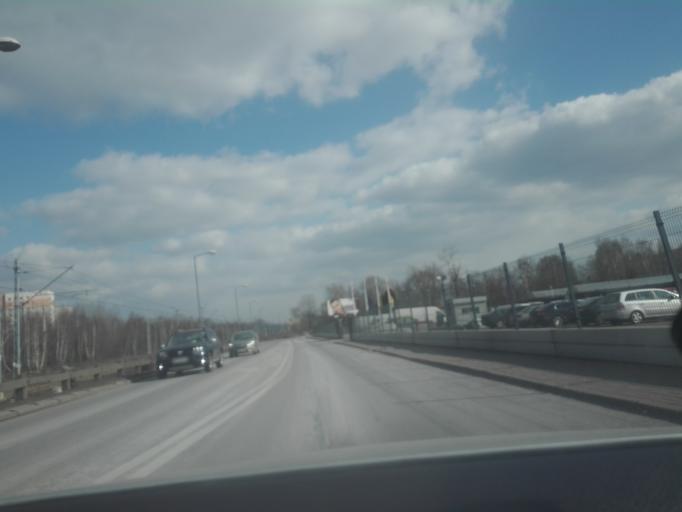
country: PL
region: Silesian Voivodeship
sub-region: Katowice
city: Katowice
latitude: 50.2632
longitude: 18.9911
